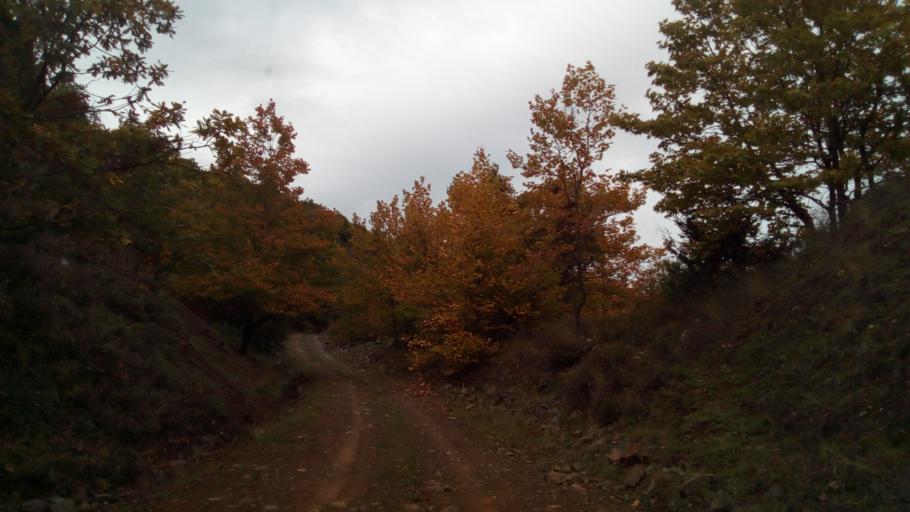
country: GR
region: West Greece
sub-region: Nomos Aitolias kai Akarnanias
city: Nafpaktos
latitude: 38.5517
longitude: 21.9699
